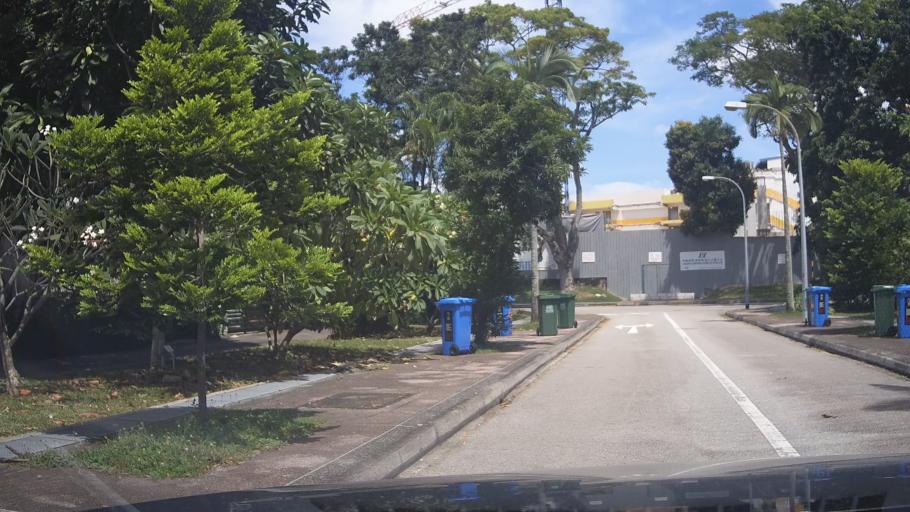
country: SG
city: Singapore
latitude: 1.3047
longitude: 103.8994
